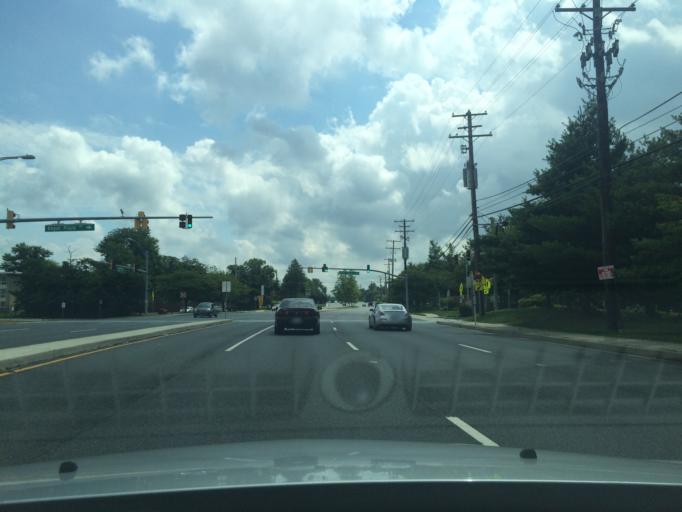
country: US
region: Maryland
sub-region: Prince George's County
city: Suitland
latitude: 38.8520
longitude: -76.9183
